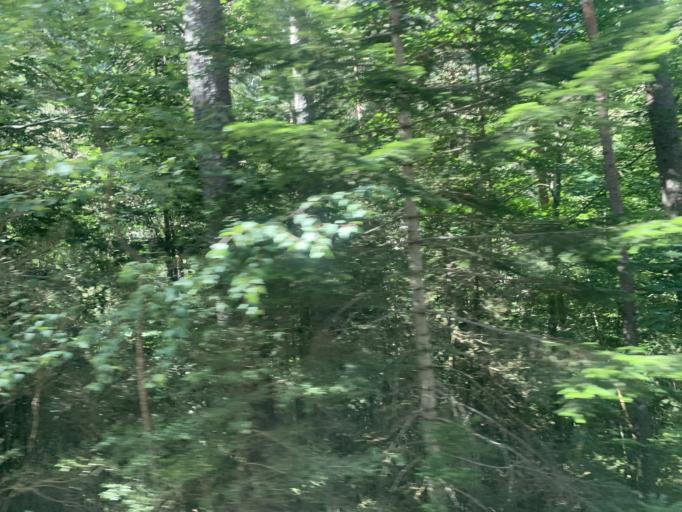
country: ES
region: Aragon
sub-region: Provincia de Huesca
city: Broto
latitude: 42.6533
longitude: -0.0772
